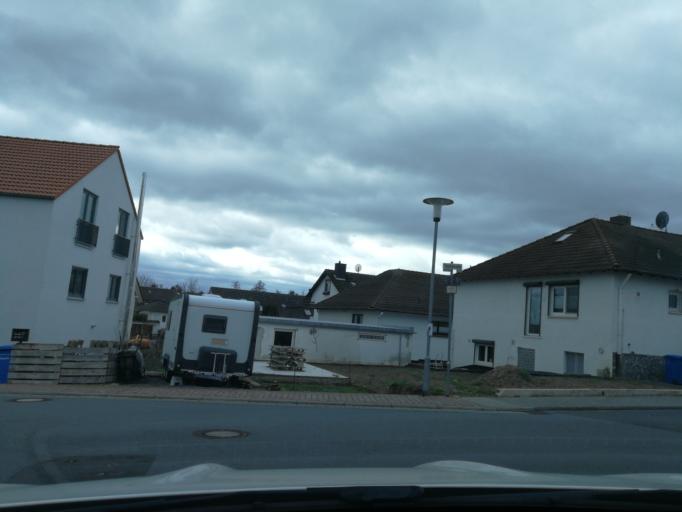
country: DE
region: Hesse
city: Reinheim
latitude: 49.8462
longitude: 8.8325
